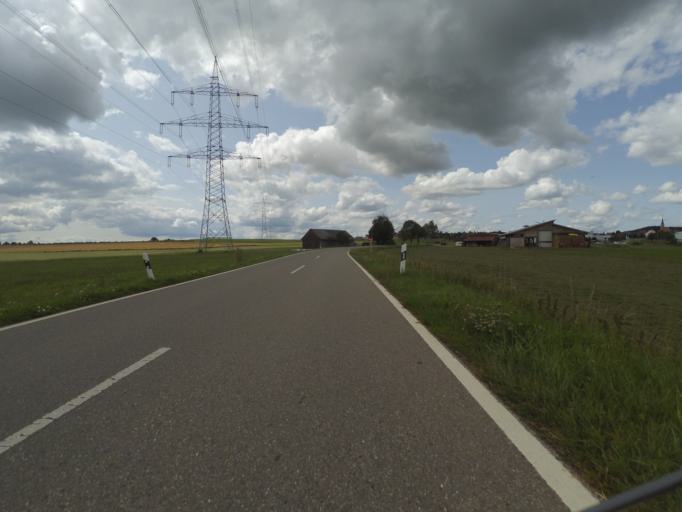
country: DE
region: Baden-Wuerttemberg
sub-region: Freiburg Region
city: Braunlingen
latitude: 47.8890
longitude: 8.4470
